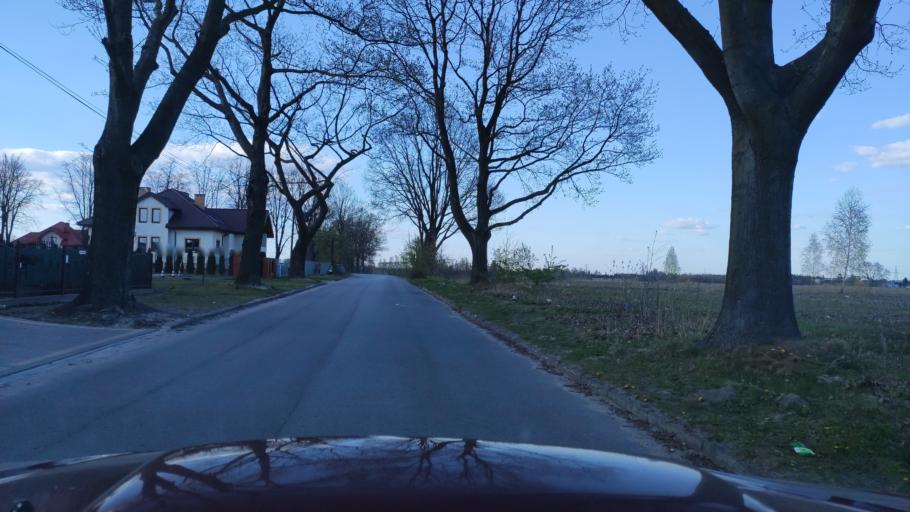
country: PL
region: Masovian Voivodeship
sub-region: Powiat zwolenski
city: Zwolen
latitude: 51.3622
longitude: 21.5760
